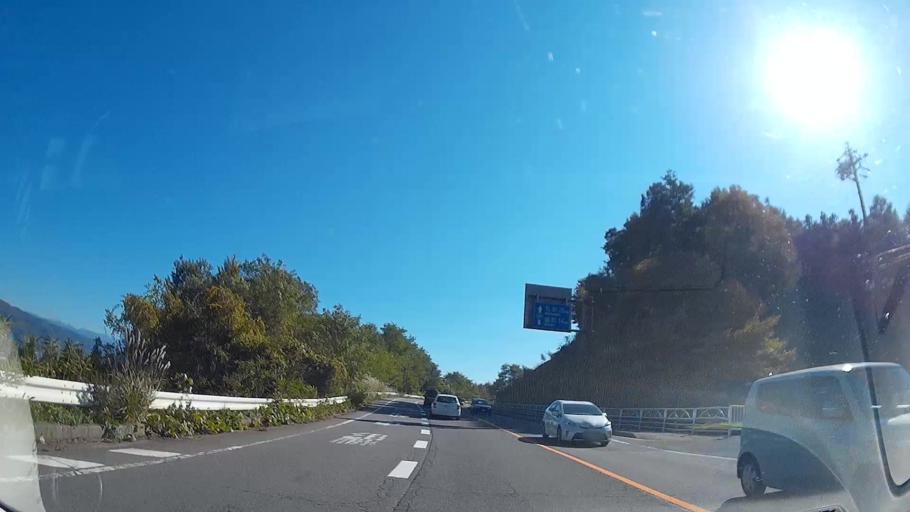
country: JP
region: Nagano
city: Okaya
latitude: 36.0821
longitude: 138.0371
